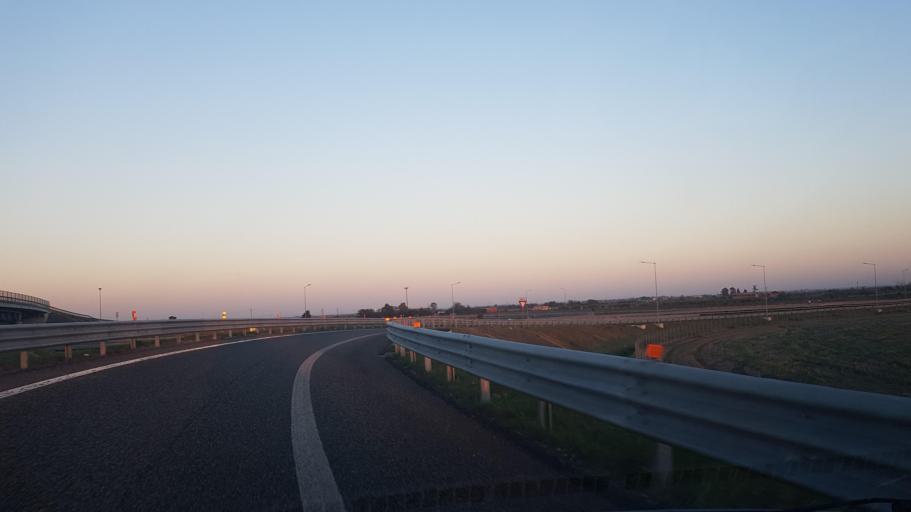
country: IT
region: Apulia
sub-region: Provincia di Foggia
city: Carapelle
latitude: 41.4289
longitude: 15.6560
